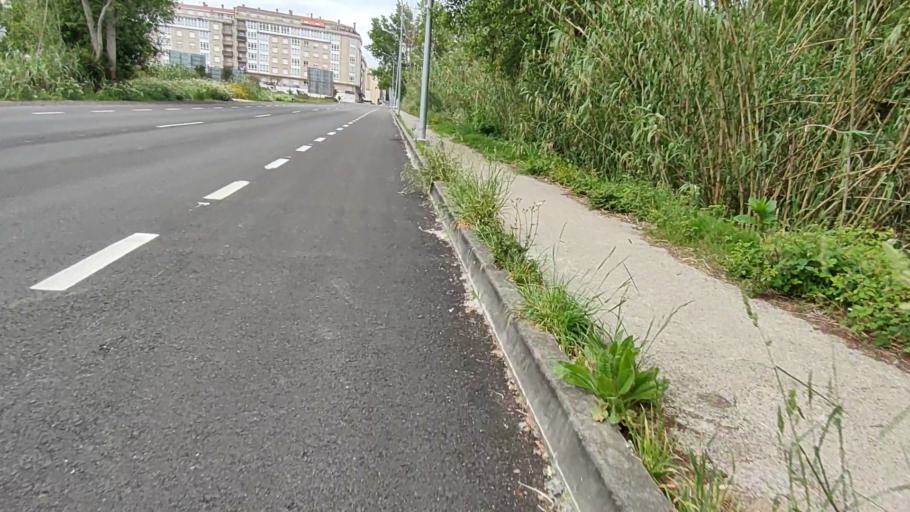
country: ES
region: Galicia
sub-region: Provincia da Coruna
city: Boiro
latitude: 42.6429
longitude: -8.8887
